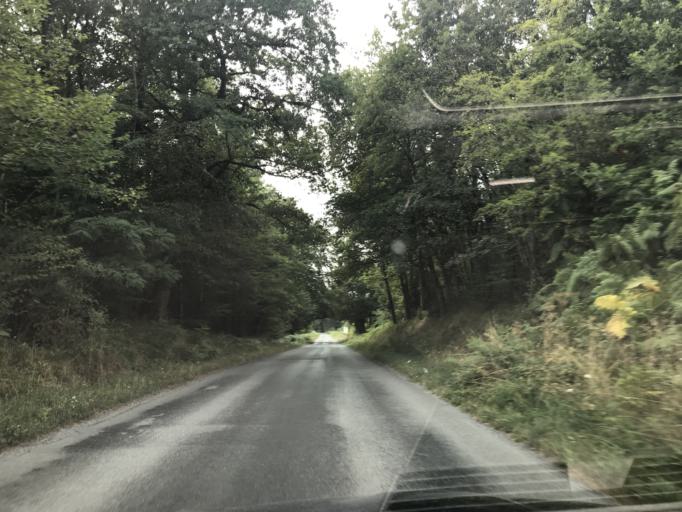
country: FR
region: Limousin
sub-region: Departement de la Correze
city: Neuvic
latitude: 45.3747
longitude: 2.2355
